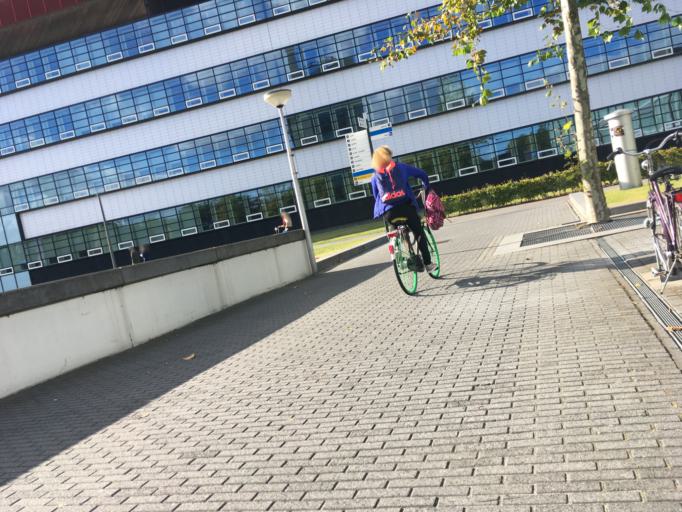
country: NL
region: Overijssel
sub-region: Gemeente Enschede
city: Enschede
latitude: 52.2383
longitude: 6.8592
